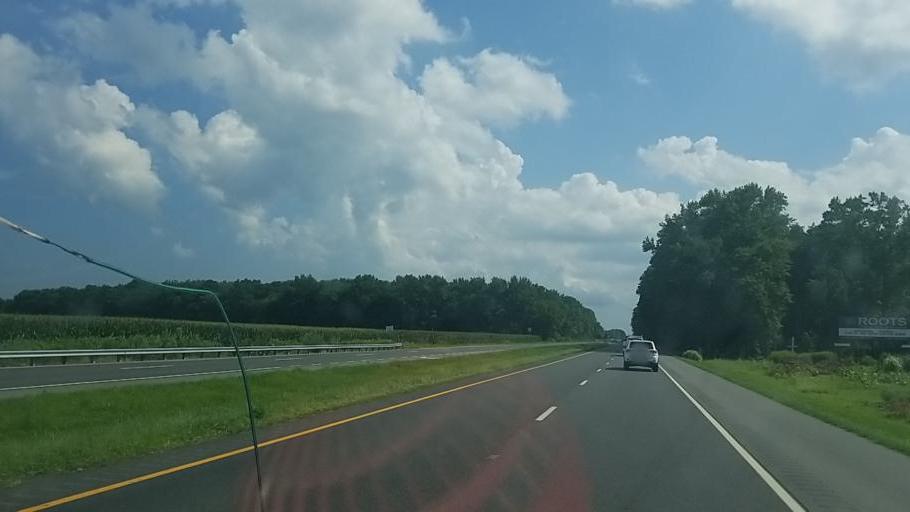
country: US
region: Delaware
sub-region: Sussex County
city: Selbyville
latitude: 38.4892
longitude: -75.2363
